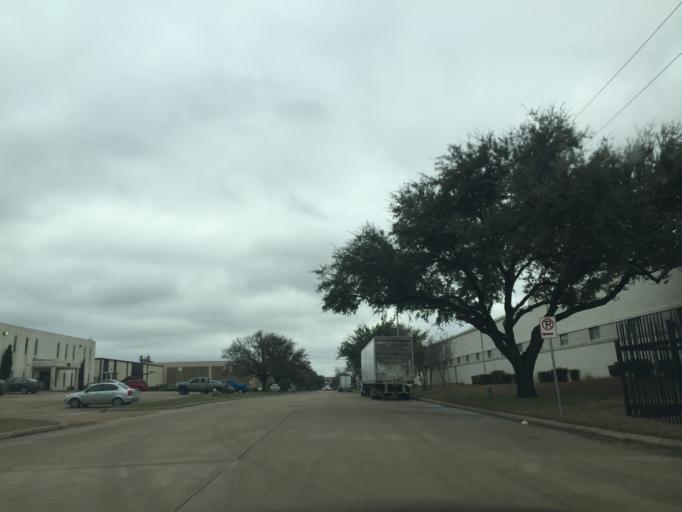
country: US
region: Texas
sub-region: Dallas County
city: Grand Prairie
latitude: 32.7542
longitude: -97.0494
